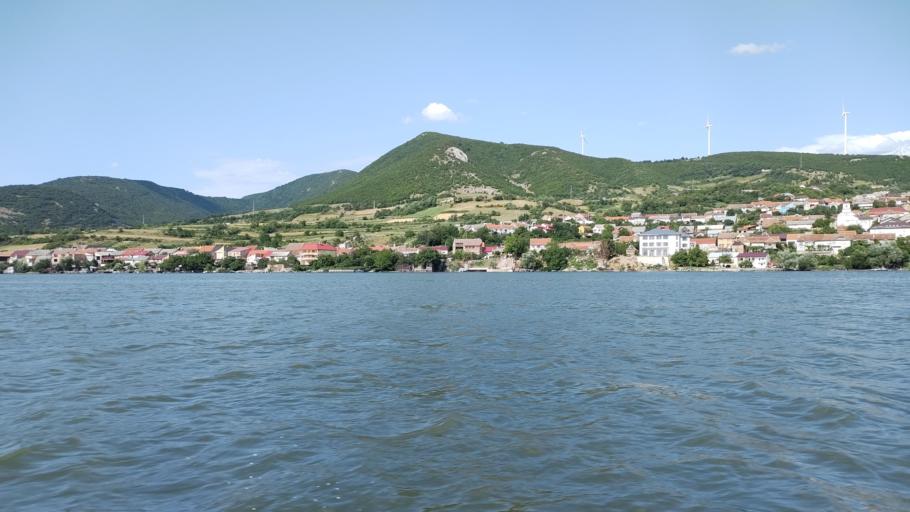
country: RO
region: Caras-Severin
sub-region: Comuna Pescari
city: Coronini
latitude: 44.6782
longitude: 21.6747
